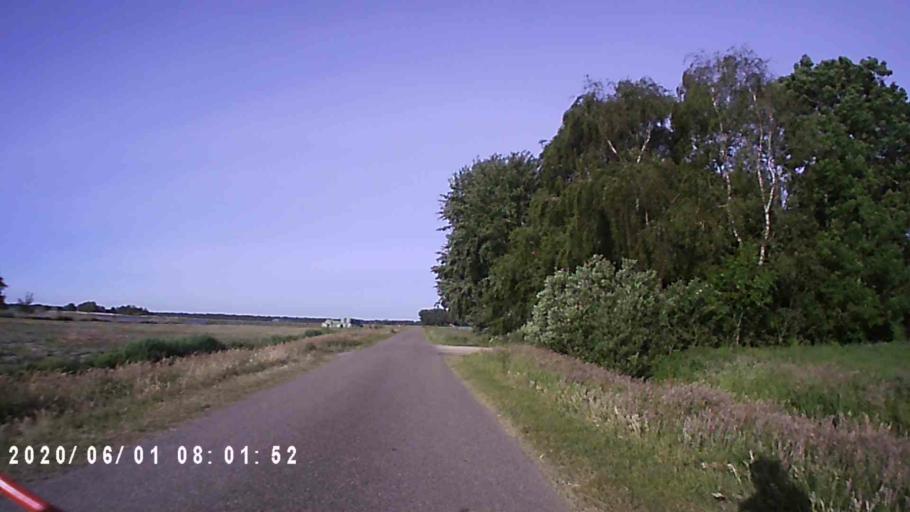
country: NL
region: Friesland
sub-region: Gemeente Dantumadiel
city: Rinsumageast
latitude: 53.2800
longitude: 5.9280
